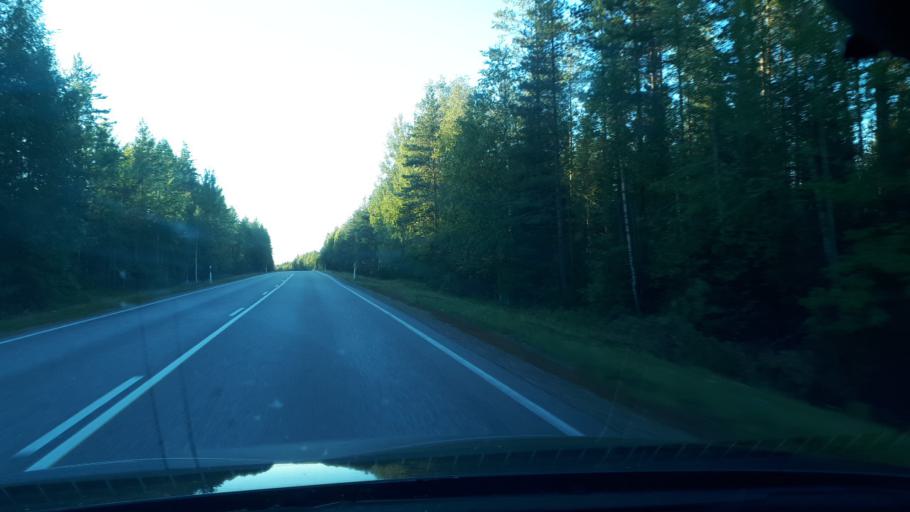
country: FI
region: Northern Savo
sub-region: Ylae-Savo
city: Kiuruvesi
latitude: 63.9273
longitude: 26.7081
